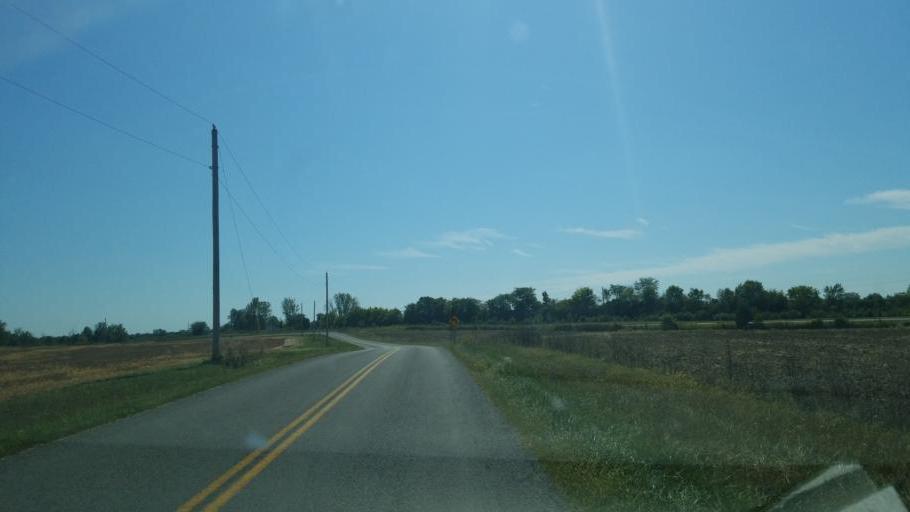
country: US
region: Ohio
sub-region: Logan County
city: Bellefontaine
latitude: 40.4280
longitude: -83.7974
